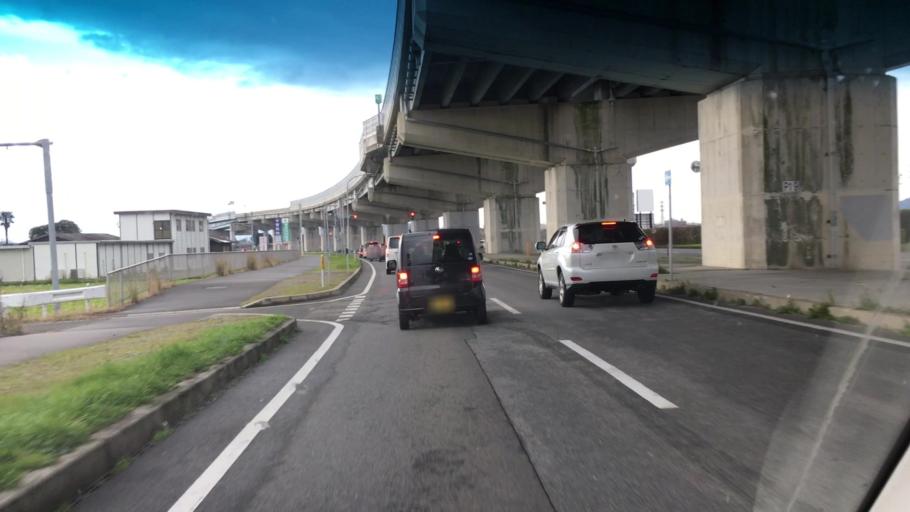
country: JP
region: Fukuoka
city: Maebaru-chuo
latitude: 33.5638
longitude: 130.2371
